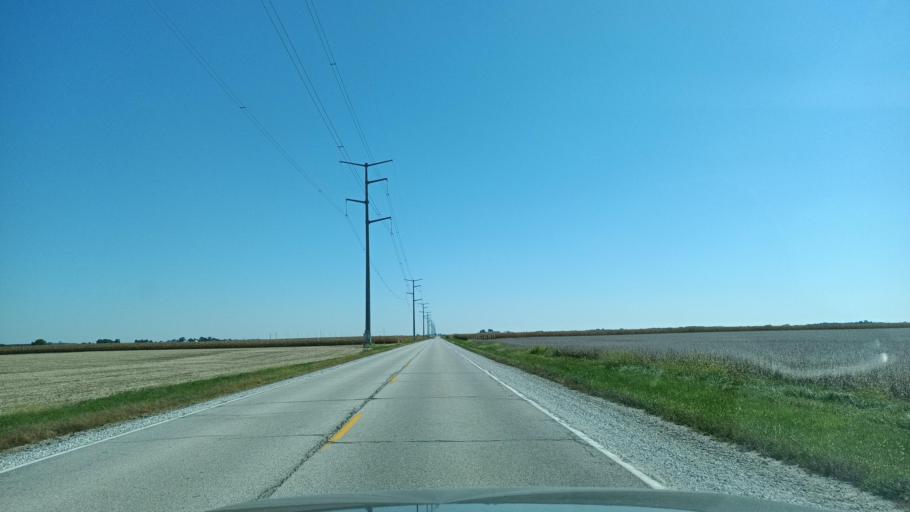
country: US
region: Illinois
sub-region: Peoria County
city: Elmwood
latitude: 40.9023
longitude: -90.0124
